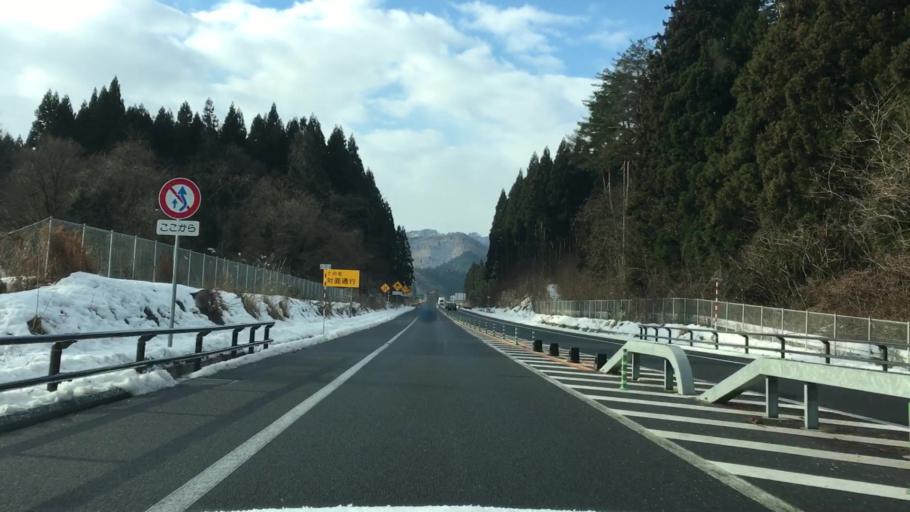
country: JP
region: Akita
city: Odate
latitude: 40.2441
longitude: 140.5096
